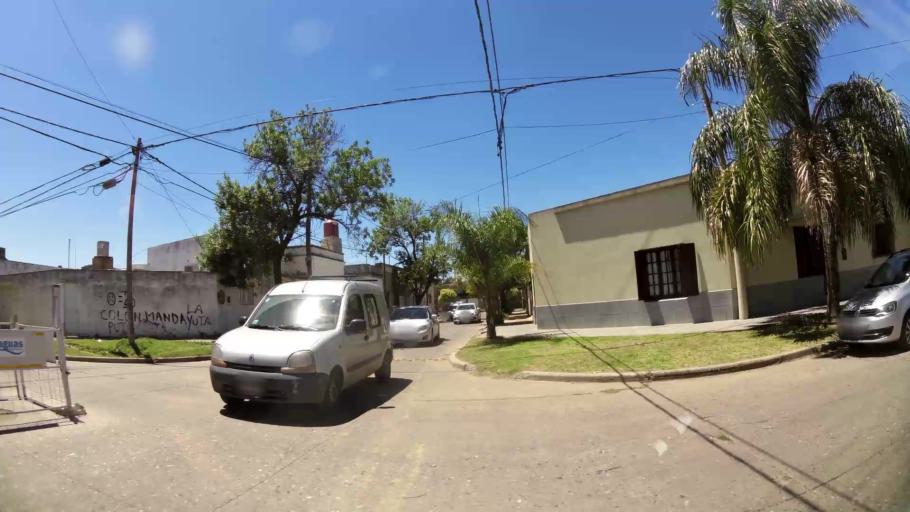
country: AR
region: Santa Fe
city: Santa Fe de la Vera Cruz
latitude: -31.6282
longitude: -60.7122
